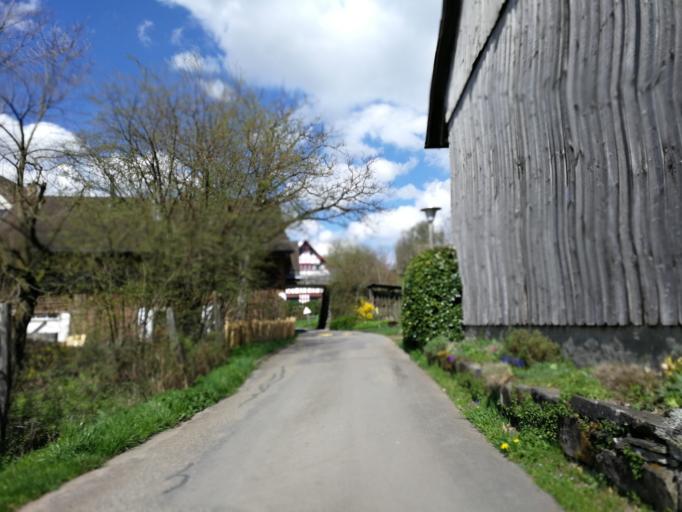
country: CH
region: Zurich
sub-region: Bezirk Hinwil
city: Wolfhausen
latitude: 47.2381
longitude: 8.7876
